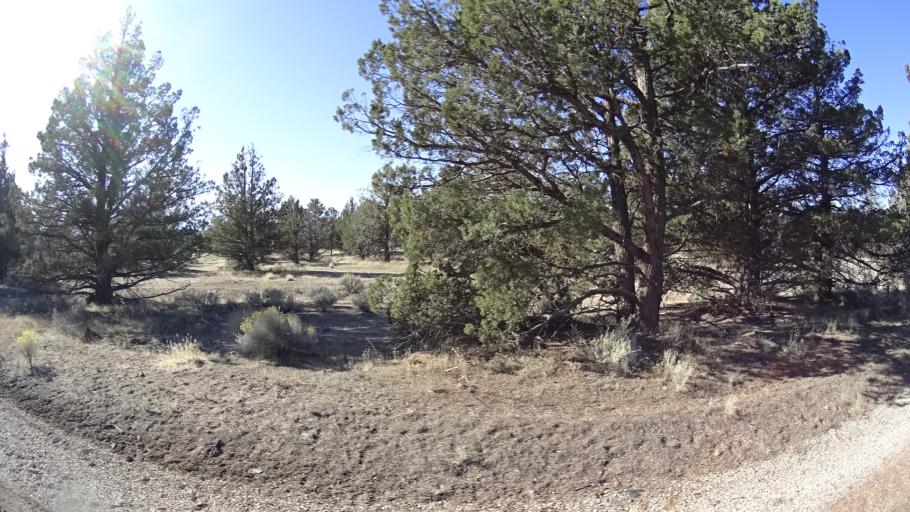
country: US
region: California
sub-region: Siskiyou County
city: Weed
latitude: 41.6095
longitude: -122.3112
